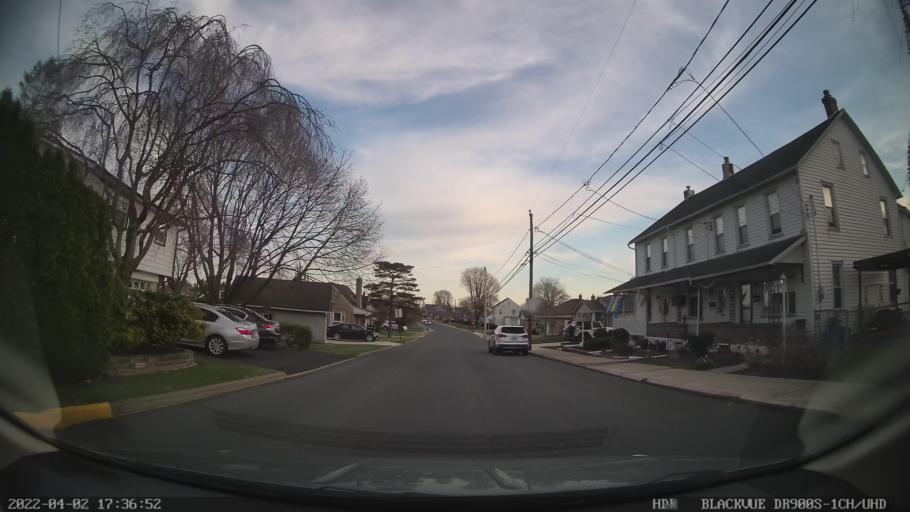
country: US
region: Pennsylvania
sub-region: Northampton County
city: Northampton
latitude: 40.6944
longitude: -75.4970
